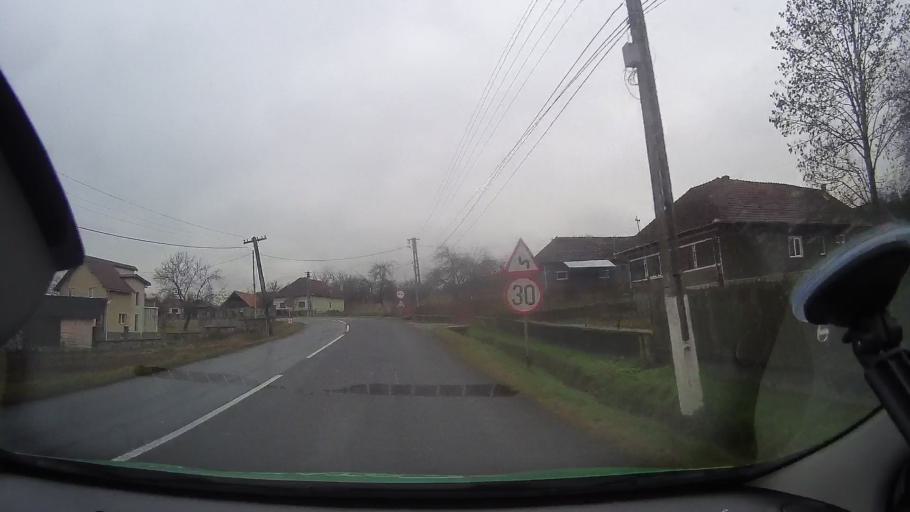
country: RO
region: Arad
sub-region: Comuna Varfurile
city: Varfurile
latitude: 46.3174
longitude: 22.5088
